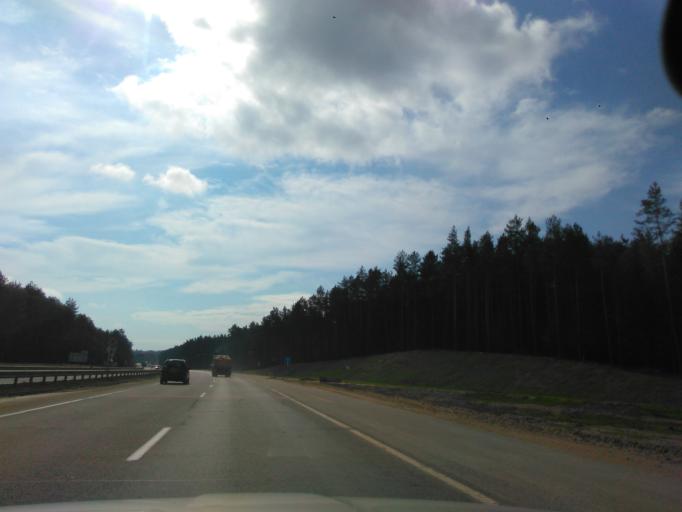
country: BY
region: Minsk
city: Rakaw
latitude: 53.9639
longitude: 27.0912
